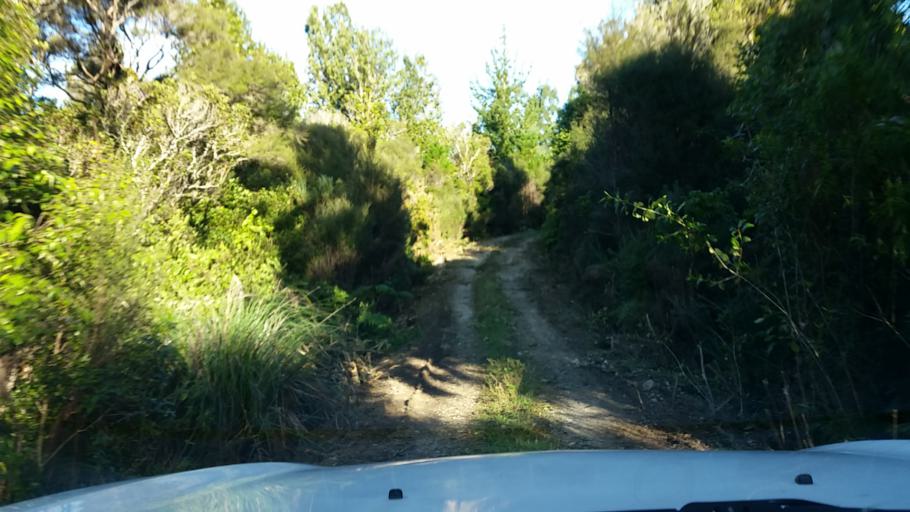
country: NZ
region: Waikato
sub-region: Otorohanga District
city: Otorohanga
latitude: -38.3067
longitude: 174.9559
